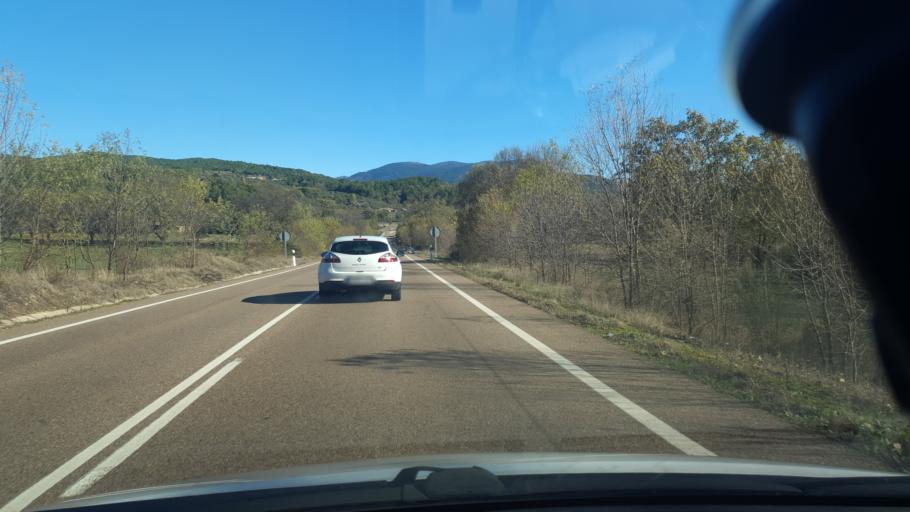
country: ES
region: Castille and Leon
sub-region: Provincia de Avila
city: Arenas de San Pedro
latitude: 40.1863
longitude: -5.0817
